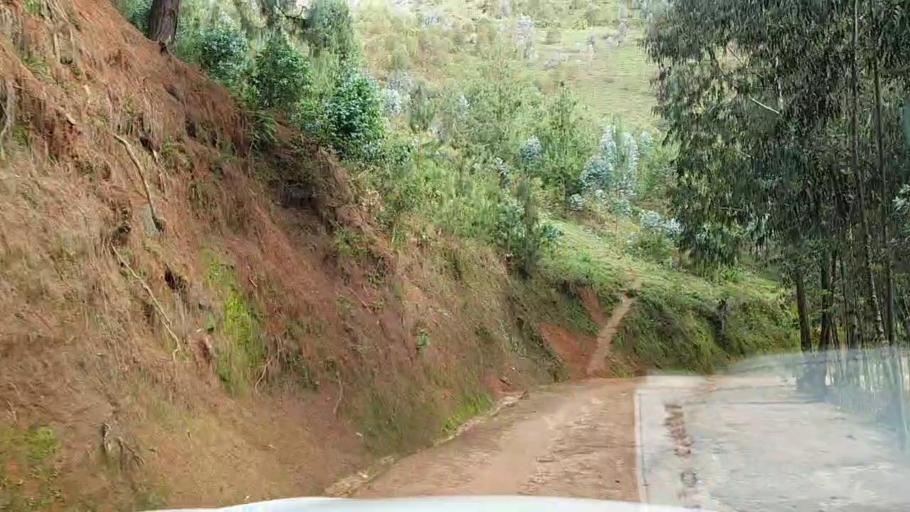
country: RW
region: Southern Province
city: Nzega
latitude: -2.4091
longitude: 29.4569
